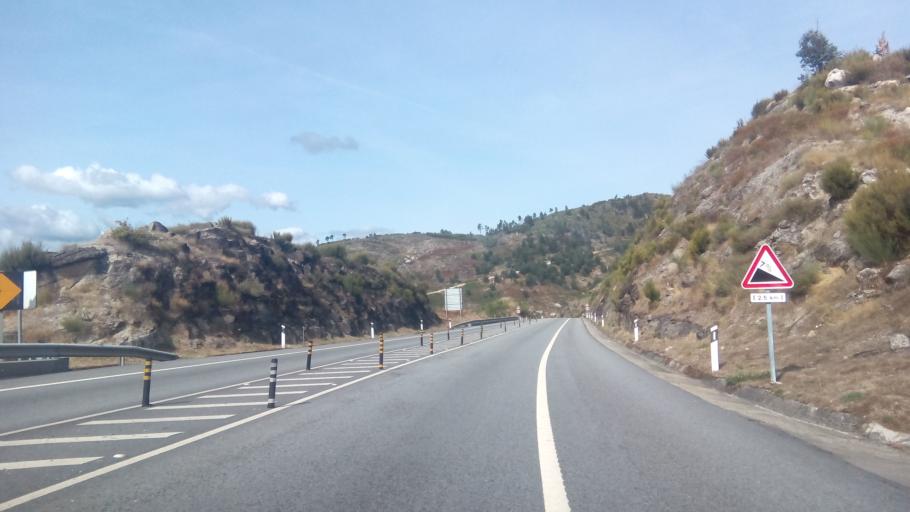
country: PT
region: Porto
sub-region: Amarante
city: Amarante
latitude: 41.2641
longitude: -7.9793
